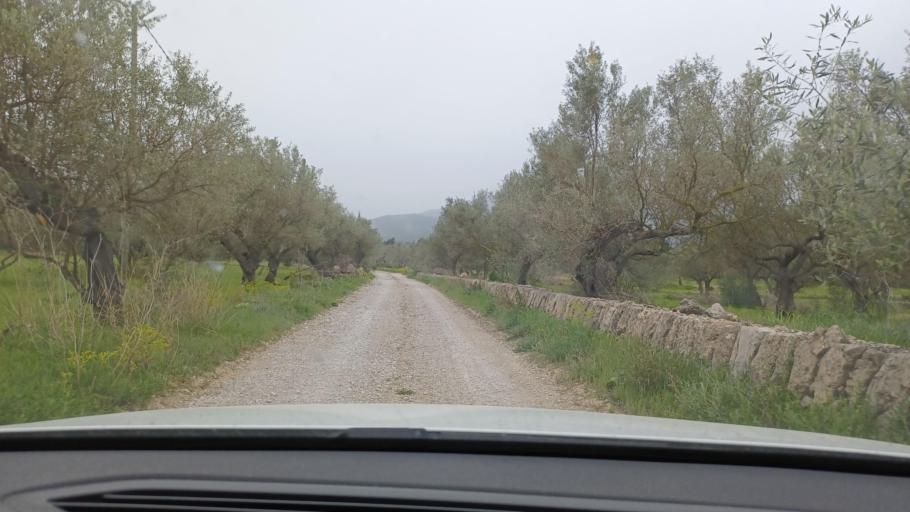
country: ES
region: Catalonia
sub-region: Provincia de Tarragona
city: Mas de Barberans
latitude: 40.8045
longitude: 0.4103
